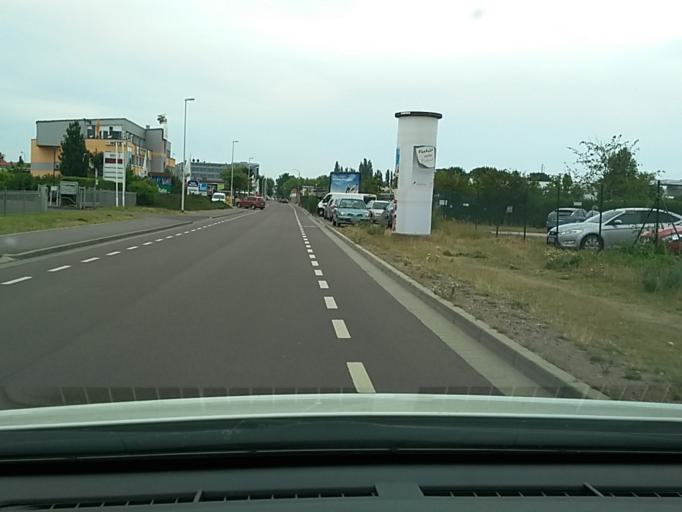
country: DE
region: Saxony-Anhalt
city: Halle (Saale)
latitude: 51.4865
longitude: 12.0021
